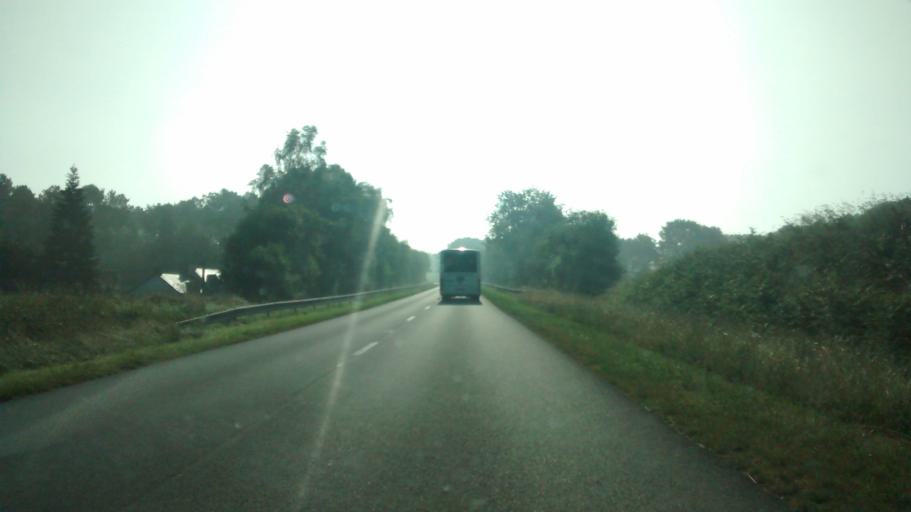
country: FR
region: Brittany
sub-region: Departement du Morbihan
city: Ruffiac
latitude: 47.8076
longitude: -2.3214
